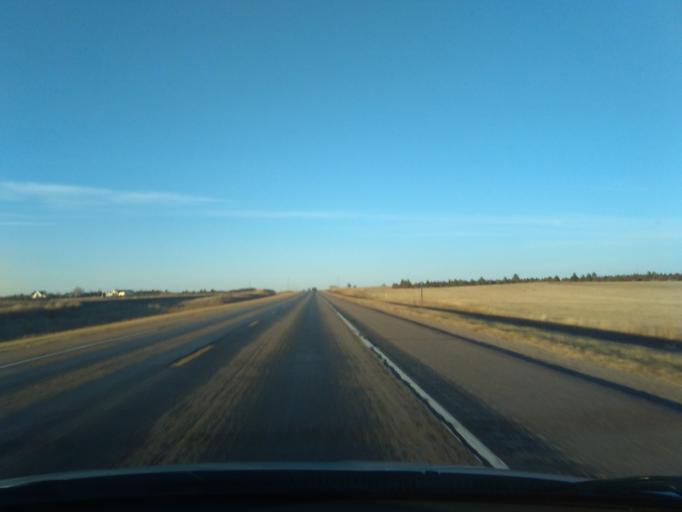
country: US
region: Nebraska
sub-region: Cheyenne County
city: Sidney
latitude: 41.1876
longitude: -102.9676
